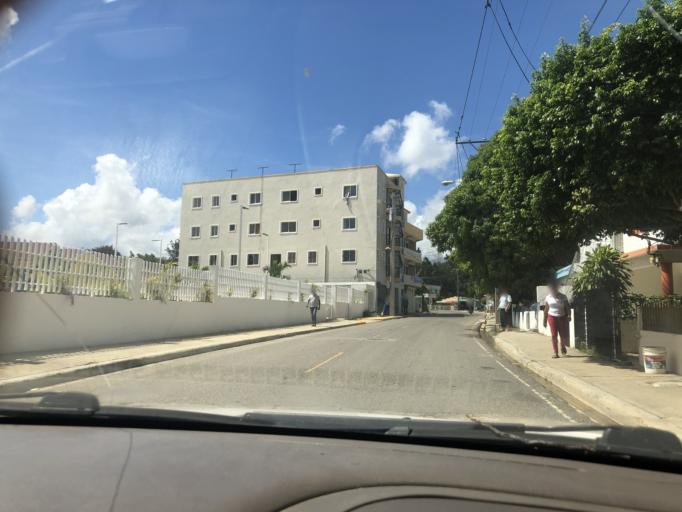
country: DO
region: Santiago
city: Santiago de los Caballeros
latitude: 19.4119
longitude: -70.7096
